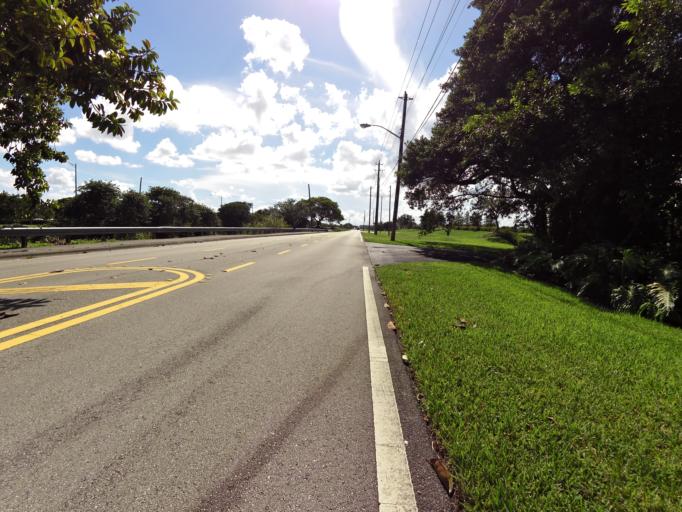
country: US
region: Florida
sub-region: Broward County
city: Cooper City
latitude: 26.0653
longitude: -80.2534
